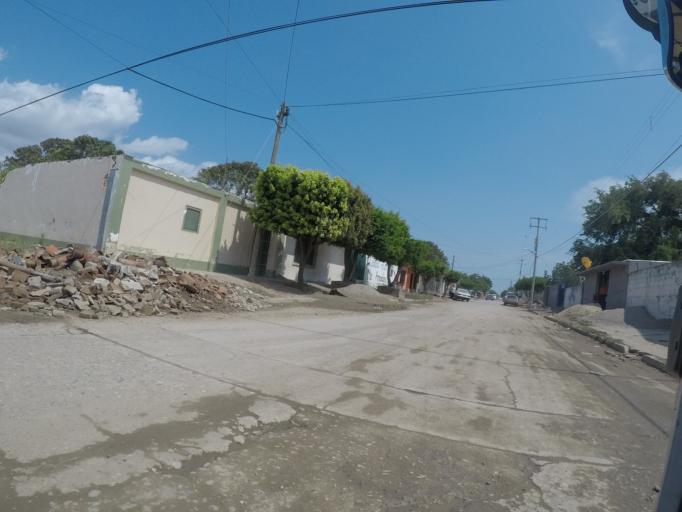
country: MX
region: Oaxaca
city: Union Hidalgo
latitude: 16.4737
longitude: -94.8354
